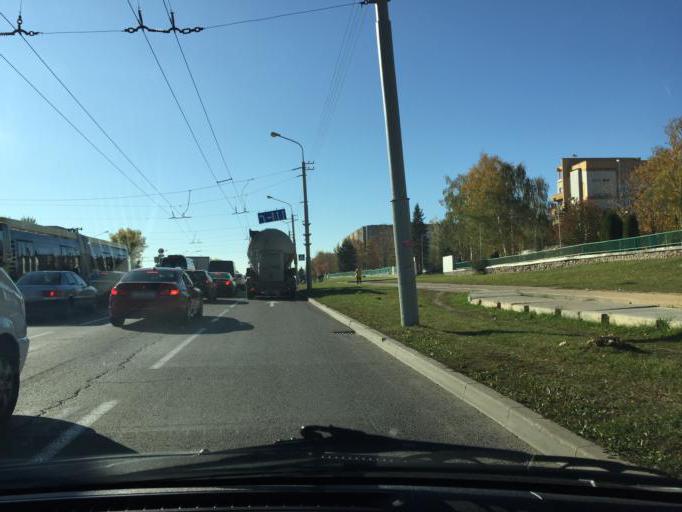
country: BY
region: Minsk
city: Syenitsa
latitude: 53.8511
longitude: 27.5370
